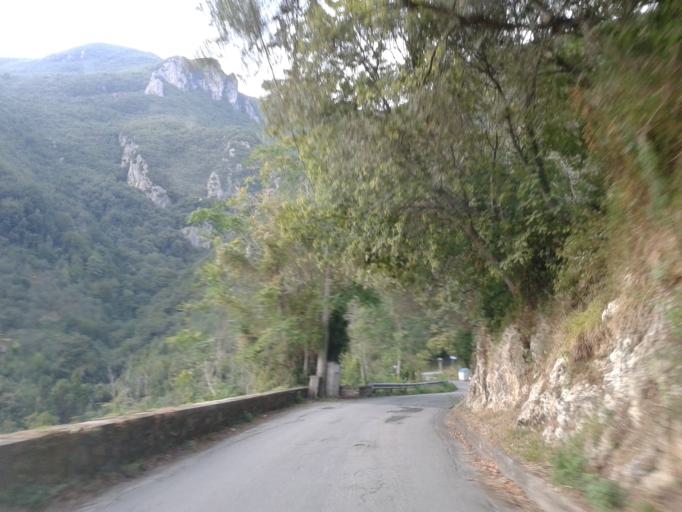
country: IT
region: Tuscany
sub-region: Provincia di Lucca
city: Pontestazzemese
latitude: 43.9551
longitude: 10.3089
